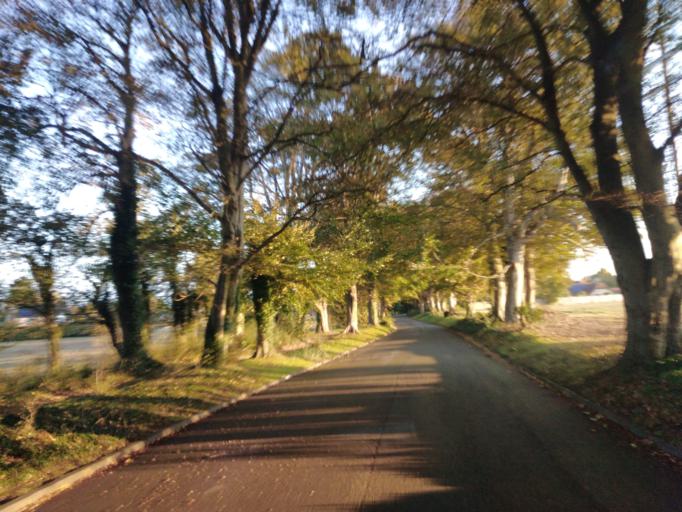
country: GB
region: England
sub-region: West Sussex
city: Rustington
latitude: 50.8197
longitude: -0.4965
